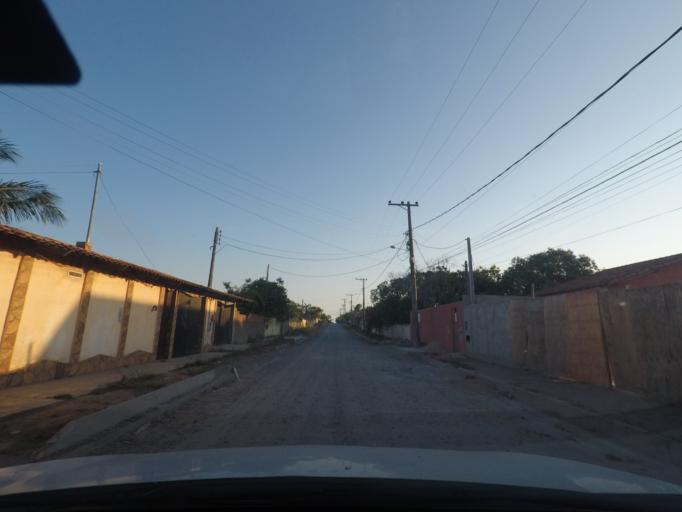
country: BR
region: Rio de Janeiro
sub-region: Marica
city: Marica
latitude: -22.9653
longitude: -42.9406
